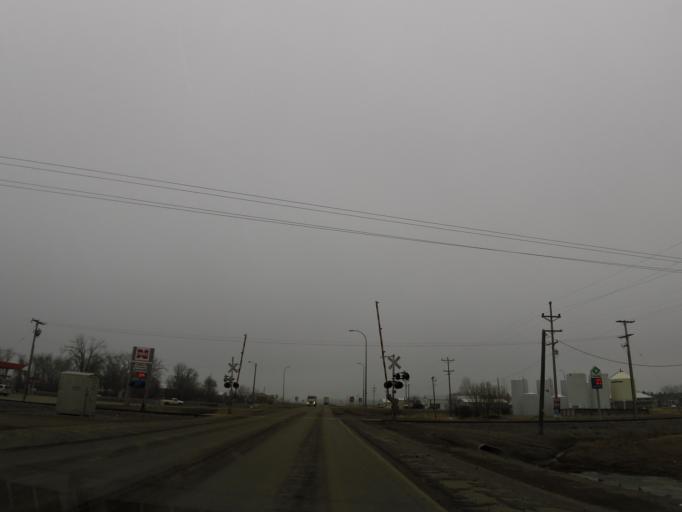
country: US
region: North Dakota
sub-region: Walsh County
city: Grafton
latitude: 48.5714
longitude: -97.1799
